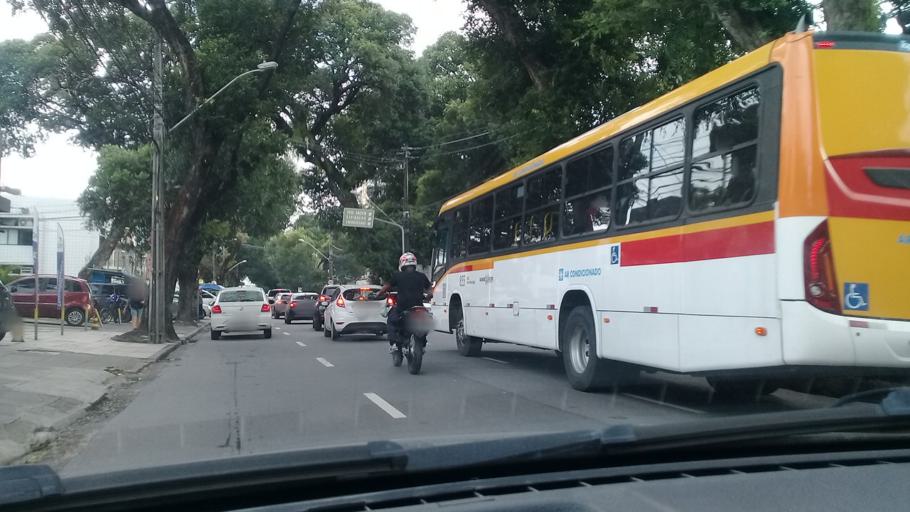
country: BR
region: Pernambuco
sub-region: Recife
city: Recife
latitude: -8.0515
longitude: -34.8879
